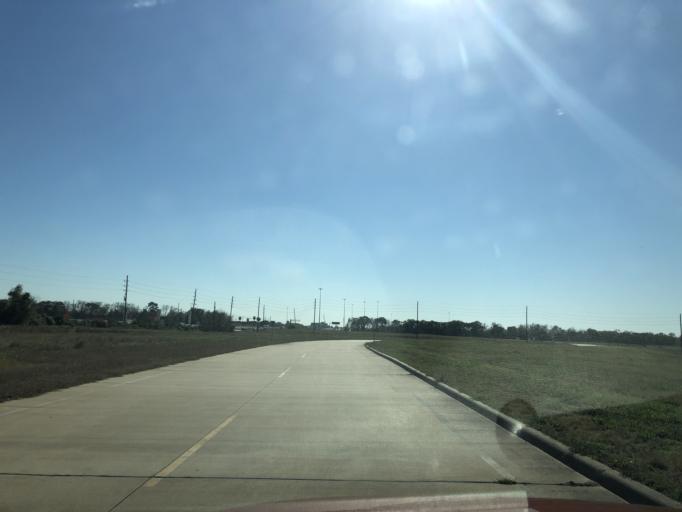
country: US
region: Texas
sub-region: Brazoria County
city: Brookside Village
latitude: 29.5909
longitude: -95.3879
